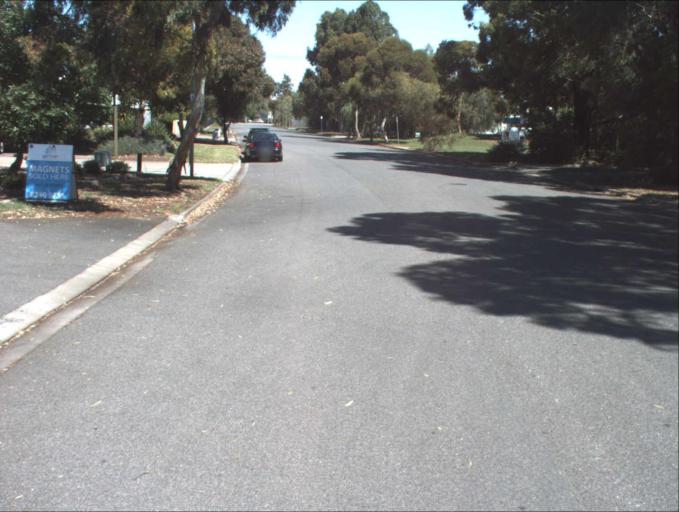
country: AU
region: South Australia
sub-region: Port Adelaide Enfield
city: Blair Athol
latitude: -34.8675
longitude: 138.5731
